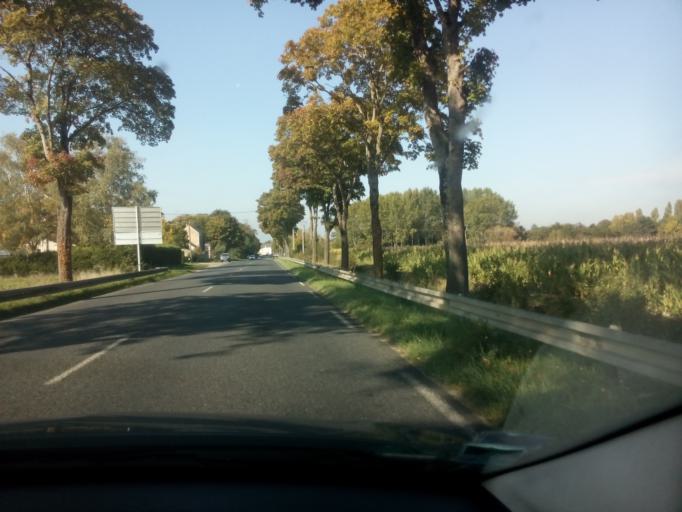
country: FR
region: Pays de la Loire
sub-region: Departement de Maine-et-Loire
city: Seiches-sur-le-Loir
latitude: 47.5711
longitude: -0.3498
